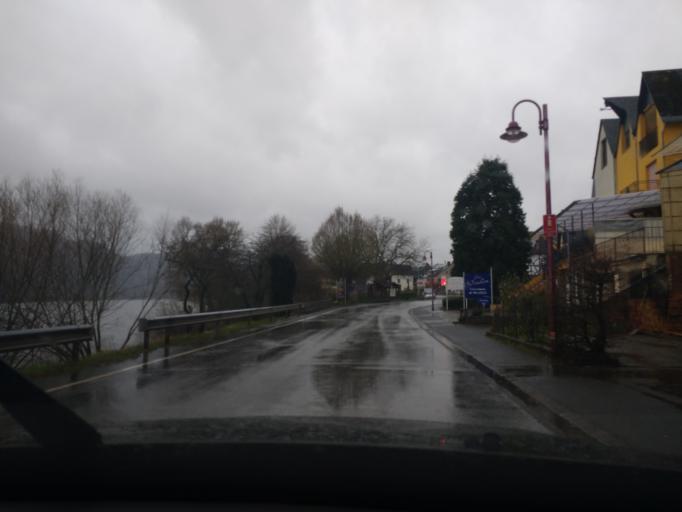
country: DE
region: Rheinland-Pfalz
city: Krov
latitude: 49.9823
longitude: 7.0927
